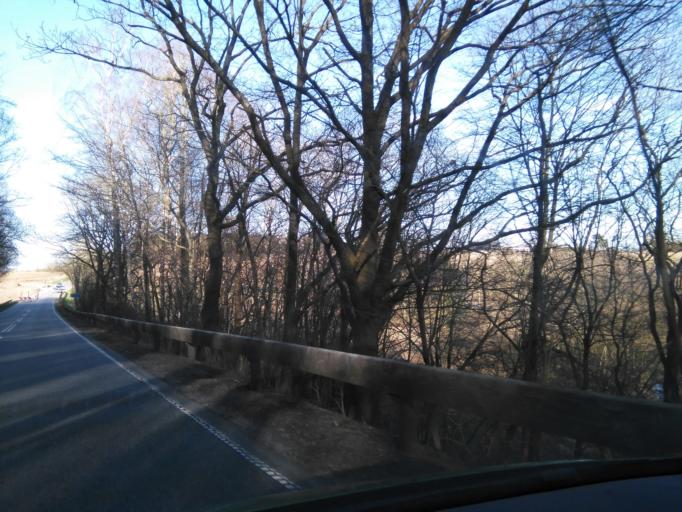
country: DK
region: Central Jutland
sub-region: Skanderborg Kommune
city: Ry
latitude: 56.0137
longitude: 9.7977
